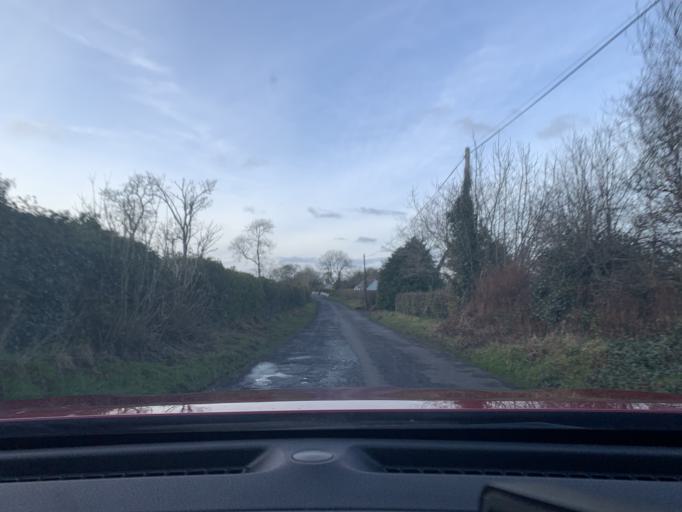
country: IE
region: Connaught
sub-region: Sligo
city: Ballymote
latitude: 54.1204
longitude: -8.5784
